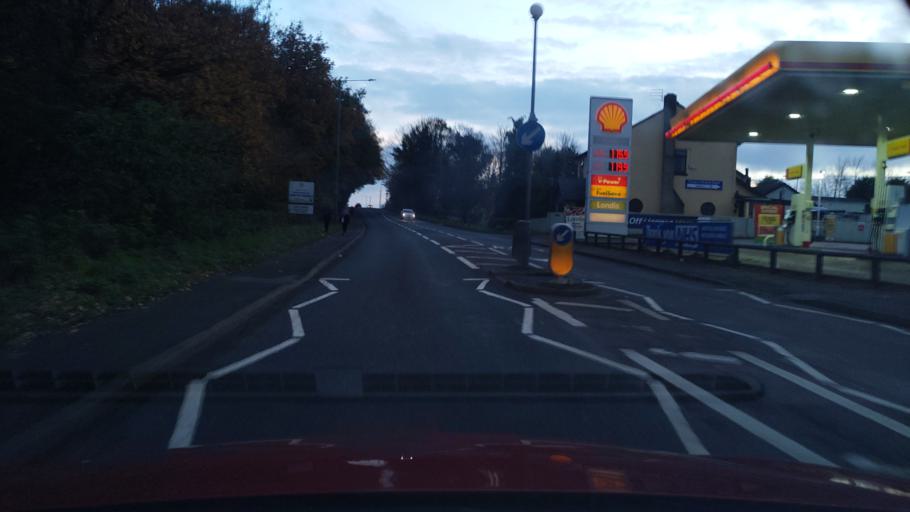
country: GB
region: England
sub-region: Lancashire
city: Clayton-le-Woods
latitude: 53.6927
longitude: -2.6745
